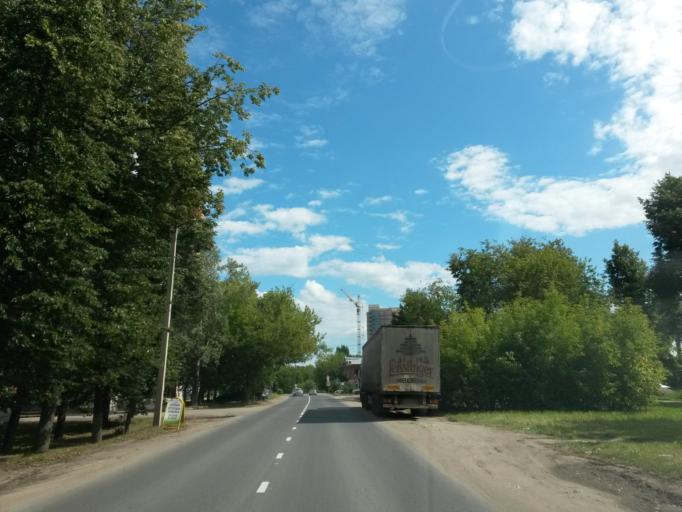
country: RU
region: Ivanovo
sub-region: Gorod Ivanovo
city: Ivanovo
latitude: 56.9896
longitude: 40.9739
